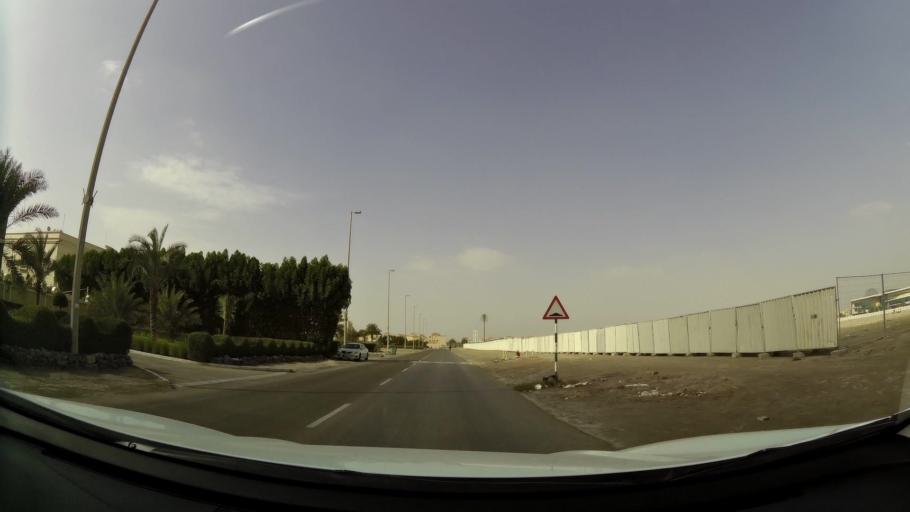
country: AE
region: Abu Dhabi
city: Abu Dhabi
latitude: 24.4264
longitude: 54.5616
